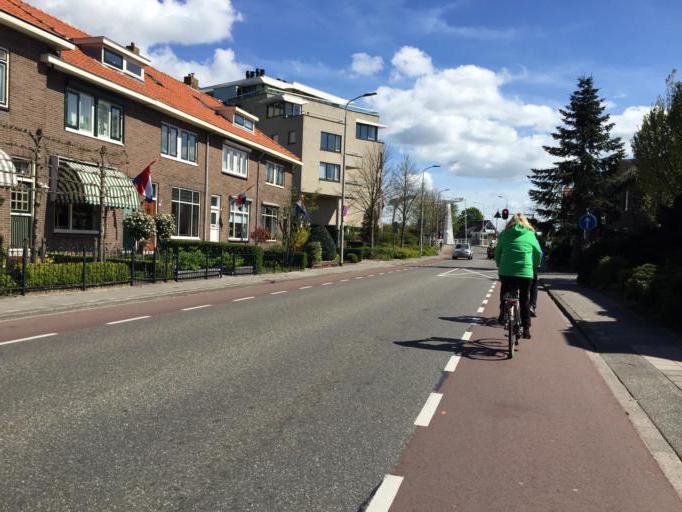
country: NL
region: South Holland
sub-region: Gemeente Lisse
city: Lisse
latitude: 52.2563
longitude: 4.5675
